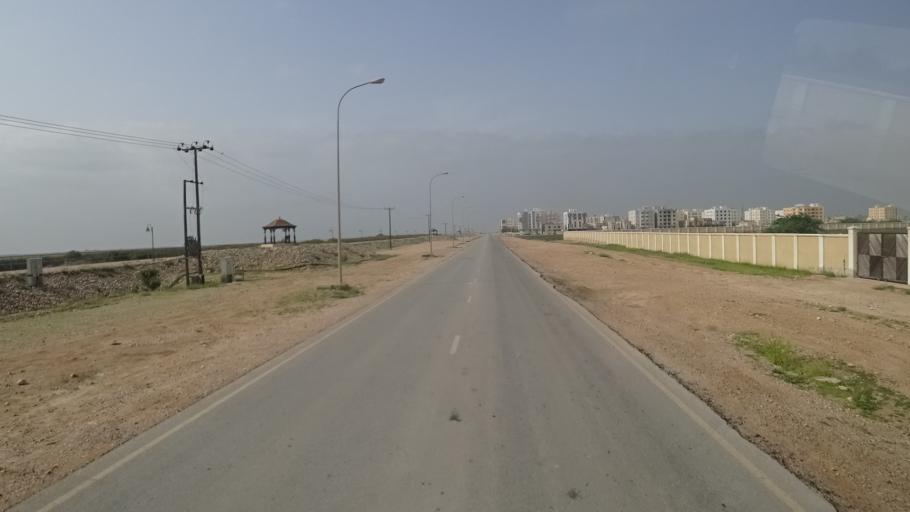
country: OM
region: Zufar
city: Salalah
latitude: 17.0204
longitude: 54.1742
